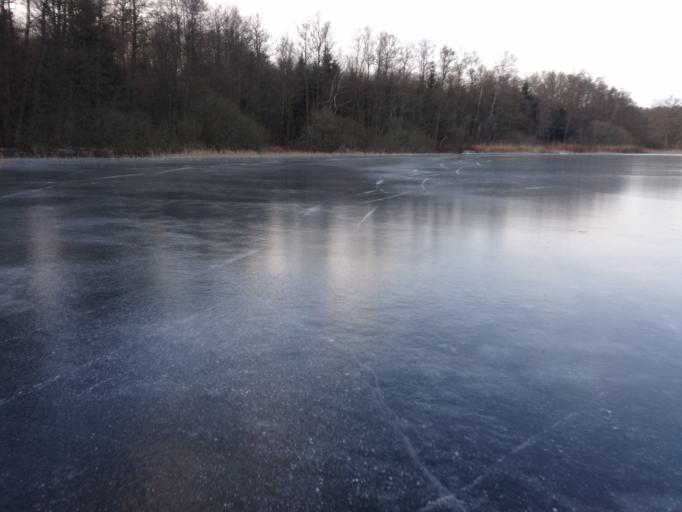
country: SE
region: Blekinge
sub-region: Karlshamns Kommun
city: Karlshamn
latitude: 56.2358
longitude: 14.9658
